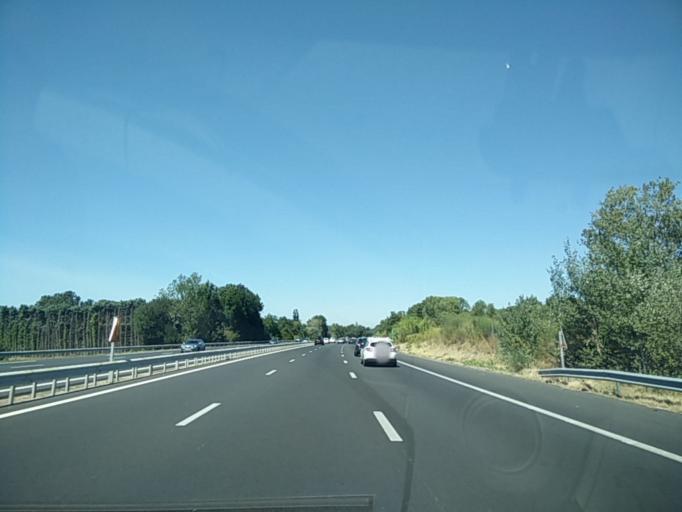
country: FR
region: Provence-Alpes-Cote d'Azur
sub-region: Departement du Vaucluse
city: Cavaillon
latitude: 43.8397
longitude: 4.9956
